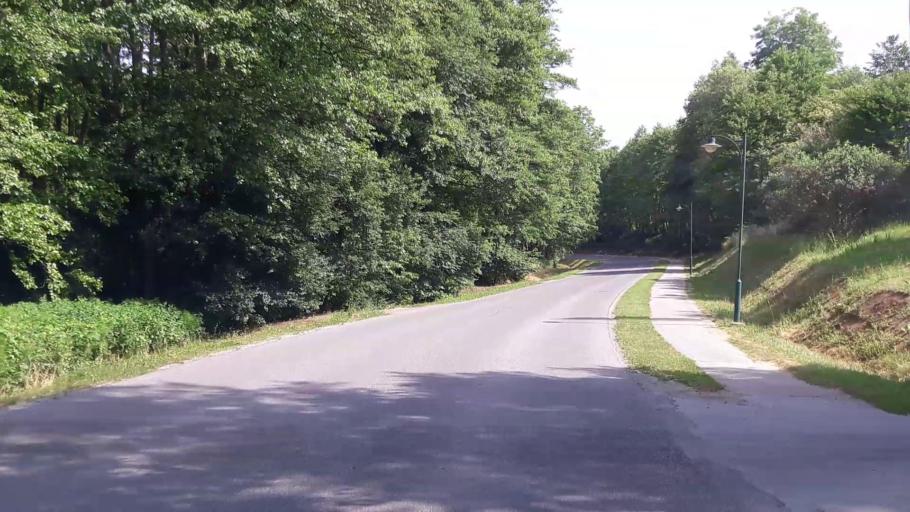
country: AT
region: Burgenland
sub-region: Politischer Bezirk Gussing
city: Stegersbach
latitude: 47.1677
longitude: 16.1487
